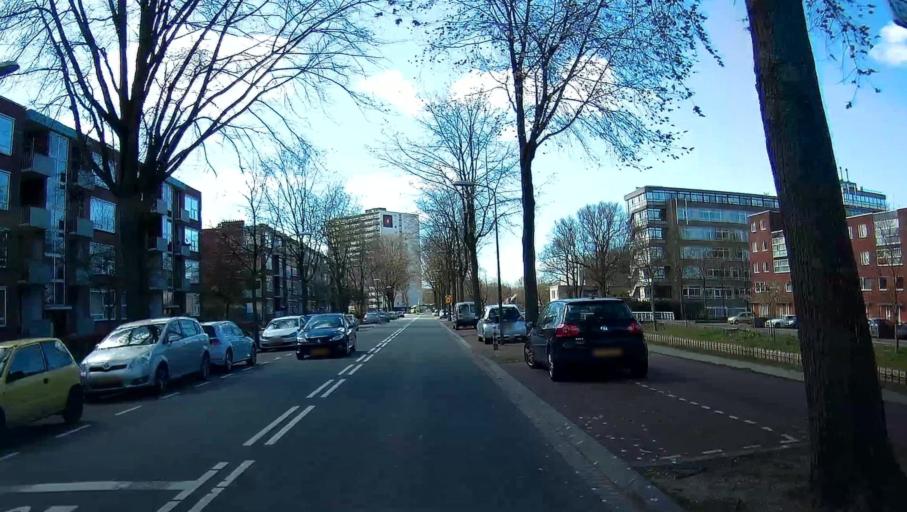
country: NL
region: South Holland
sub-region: Gemeente Westland
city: Kwintsheul
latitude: 52.0396
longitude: 4.2538
